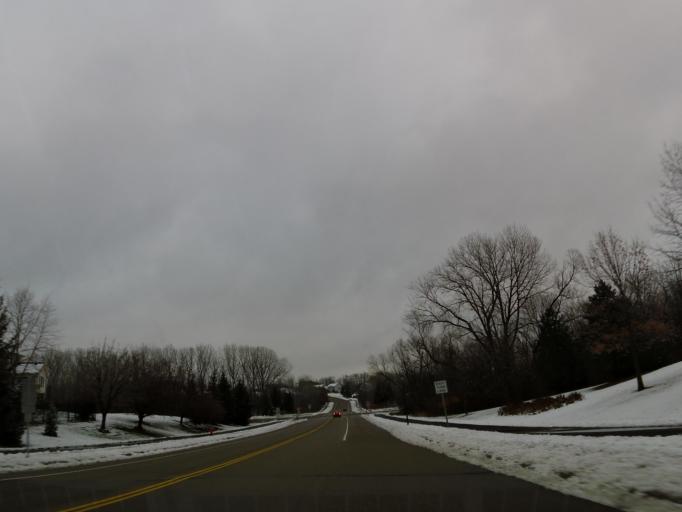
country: US
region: Minnesota
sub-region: Dakota County
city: Apple Valley
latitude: 44.7102
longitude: -93.2399
